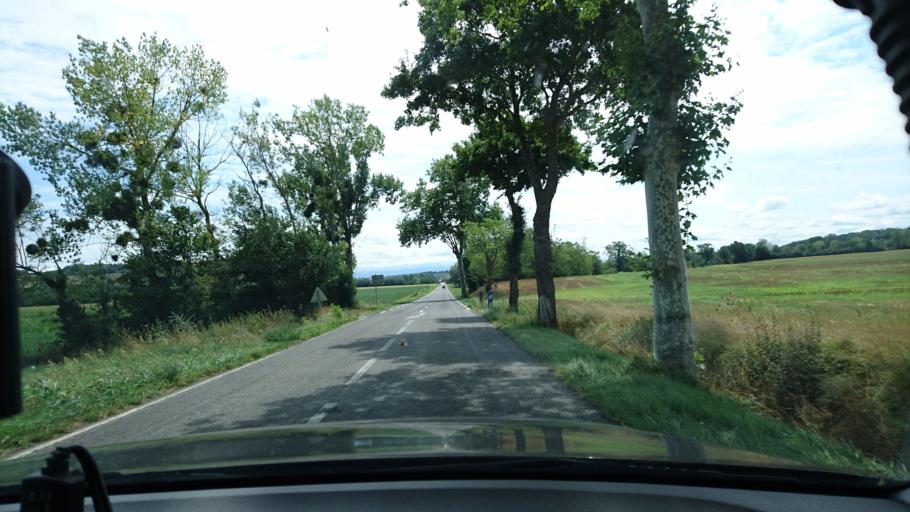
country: FR
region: Midi-Pyrenees
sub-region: Departement de l'Ariege
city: Lezat-sur-Leze
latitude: 43.2234
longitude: 1.3800
